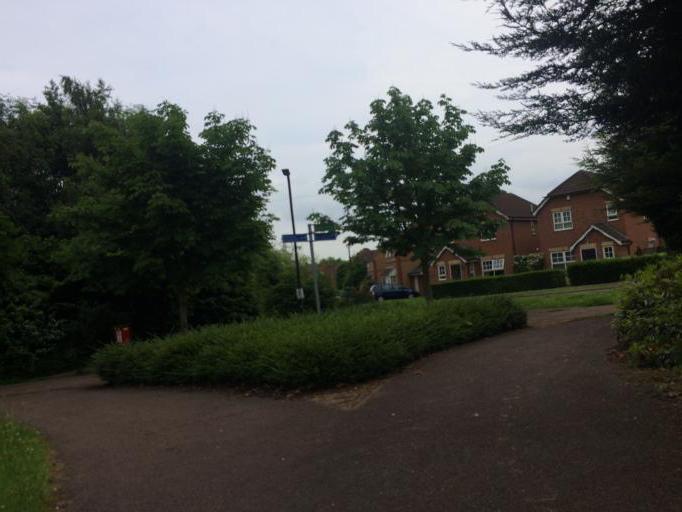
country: GB
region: England
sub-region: Milton Keynes
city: Milton Keynes
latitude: 52.0339
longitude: -0.7614
